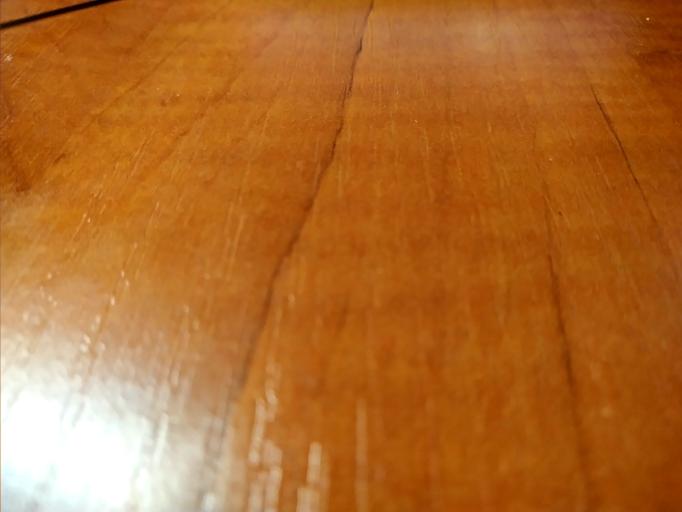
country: RU
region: Tverskaya
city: Spirovo
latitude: 57.3773
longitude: 34.9806
